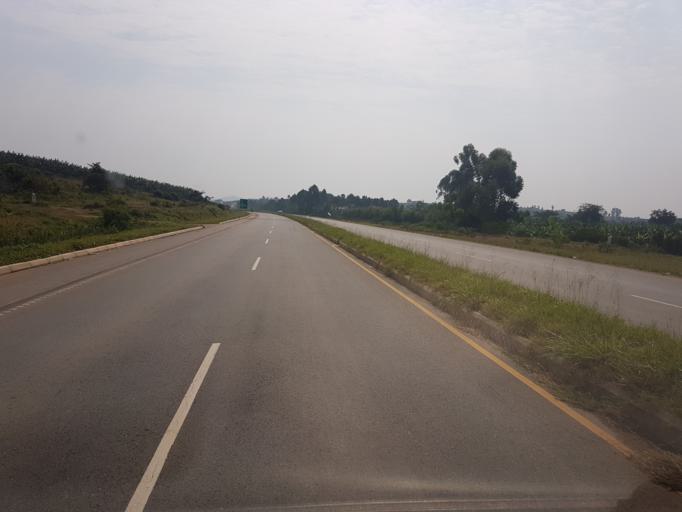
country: UG
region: Western Region
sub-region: Mbarara District
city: Bwizibwera
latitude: -0.6348
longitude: 30.5973
